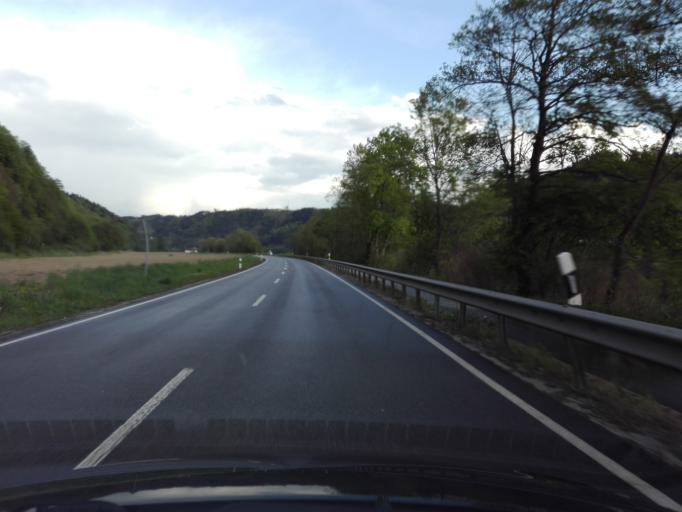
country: DE
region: Bavaria
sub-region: Lower Bavaria
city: Thyrnau
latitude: 48.5704
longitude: 13.5528
